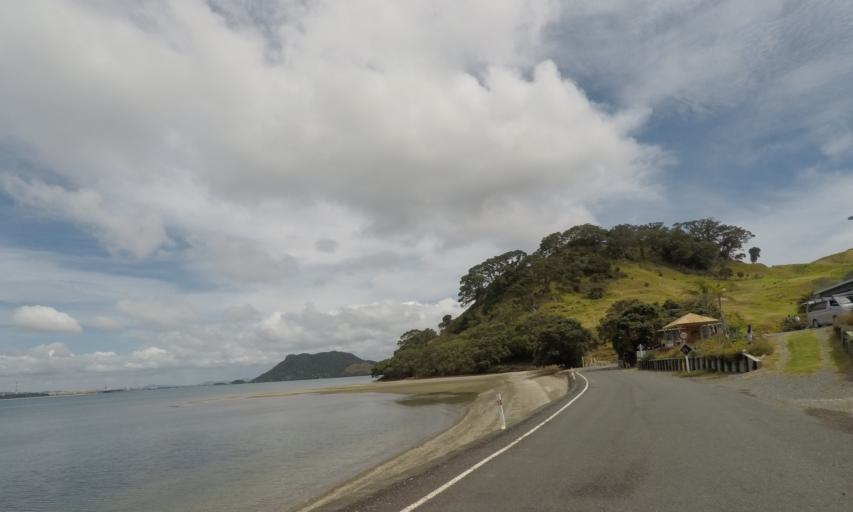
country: NZ
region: Northland
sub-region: Whangarei
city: Ruakaka
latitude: -35.8413
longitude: 174.5362
